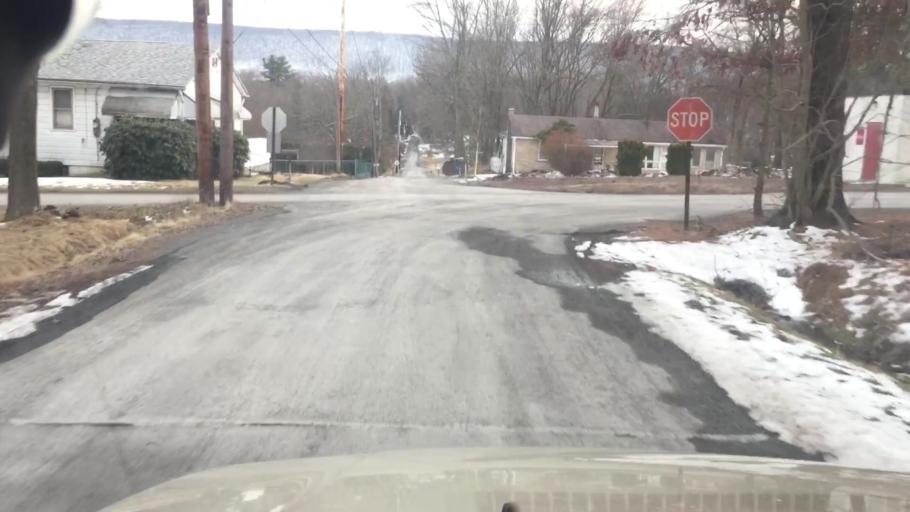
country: US
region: Pennsylvania
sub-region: Luzerne County
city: Freeland
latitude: 41.0500
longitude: -75.9565
